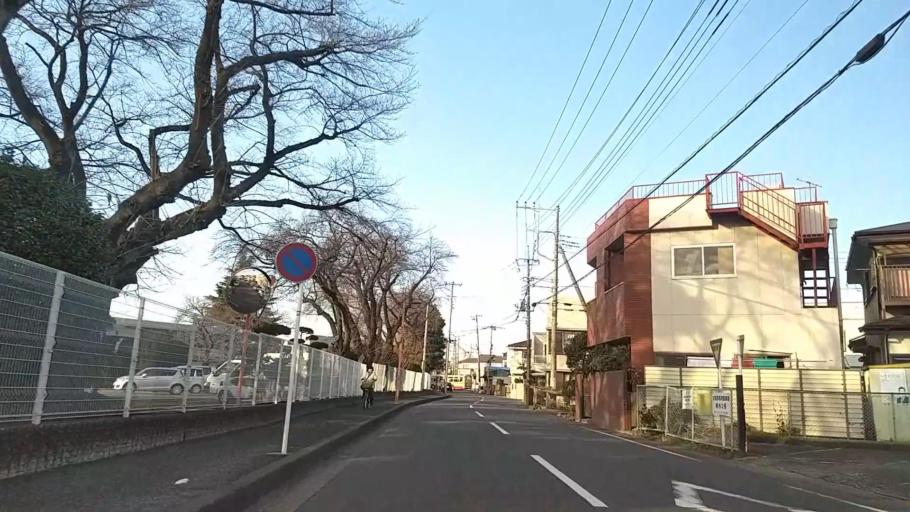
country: JP
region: Kanagawa
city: Atsugi
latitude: 35.4443
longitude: 139.3474
